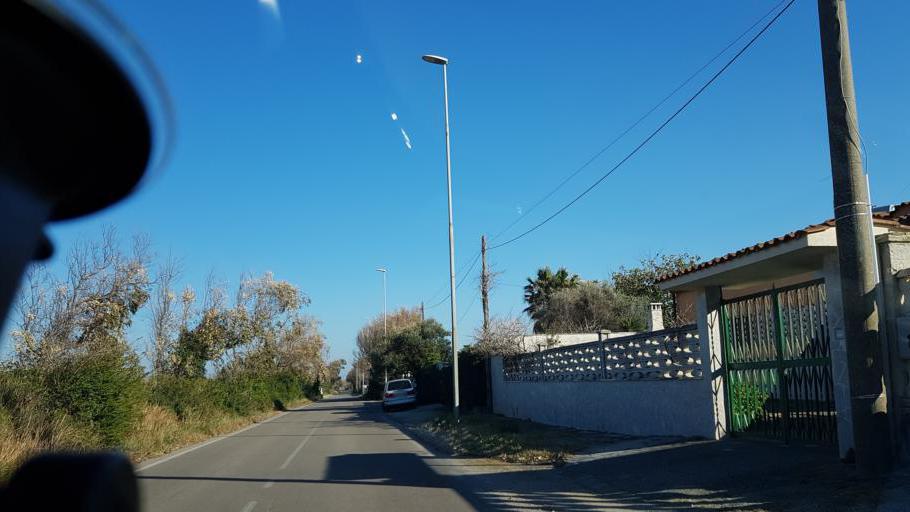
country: IT
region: Apulia
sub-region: Provincia di Lecce
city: Giorgilorio
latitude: 40.4532
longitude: 18.2174
